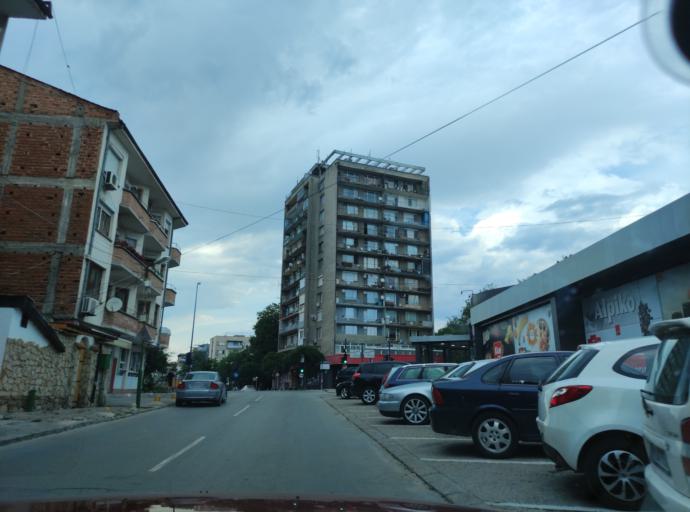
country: BG
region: Pazardzhik
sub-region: Obshtina Pazardzhik
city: Pazardzhik
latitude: 42.1858
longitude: 24.3347
